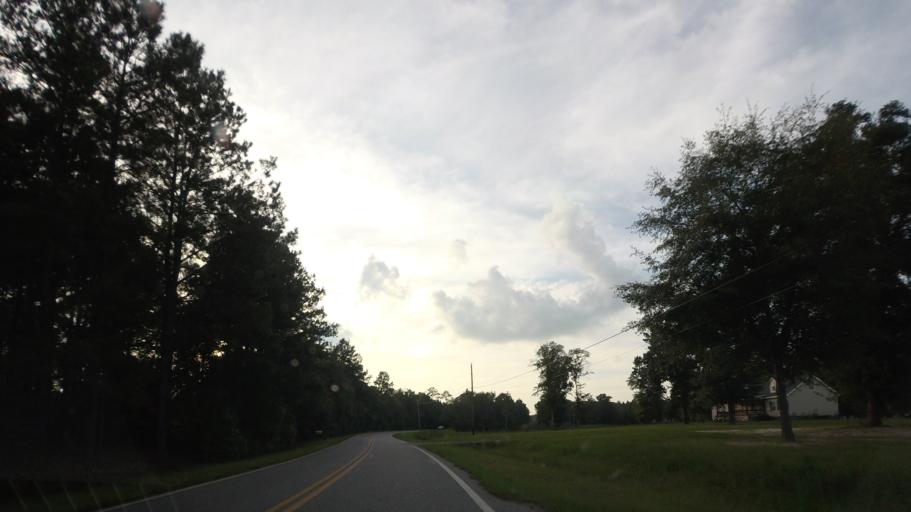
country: US
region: Georgia
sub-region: Wilkinson County
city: Gordon
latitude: 32.8630
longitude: -83.4615
